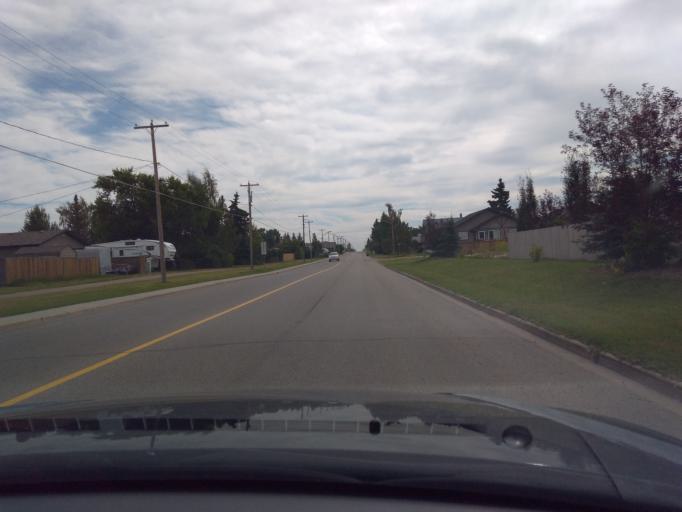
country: CA
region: Alberta
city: Didsbury
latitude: 51.6567
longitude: -114.1429
